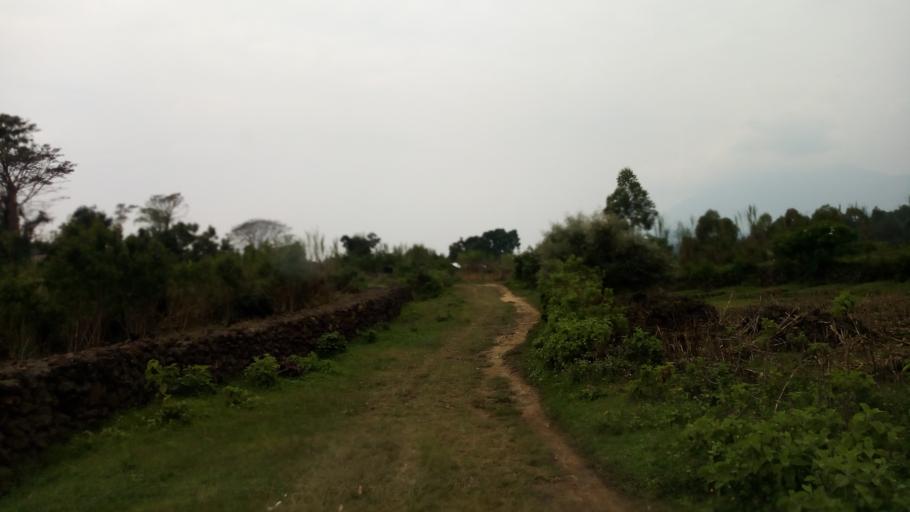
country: UG
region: Western Region
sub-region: Kisoro District
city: Kisoro
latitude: -1.2654
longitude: 29.6085
